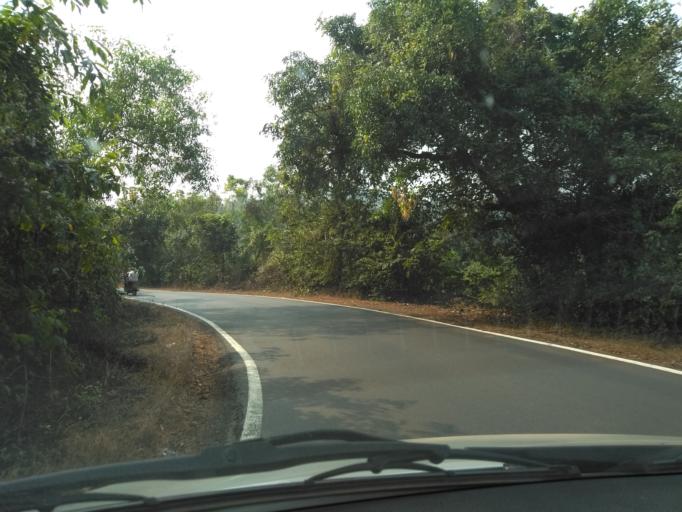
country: IN
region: Goa
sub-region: North Goa
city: Pernem
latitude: 15.7648
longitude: 73.9203
